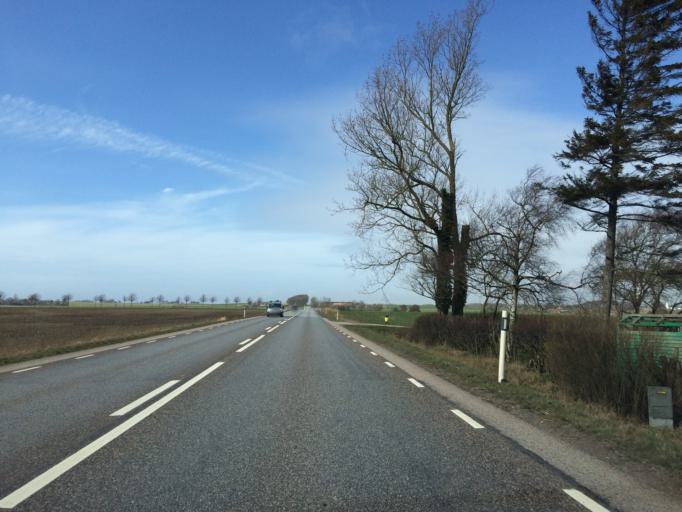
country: SE
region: Halland
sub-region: Laholms Kommun
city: Veinge
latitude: 56.5798
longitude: 13.0052
